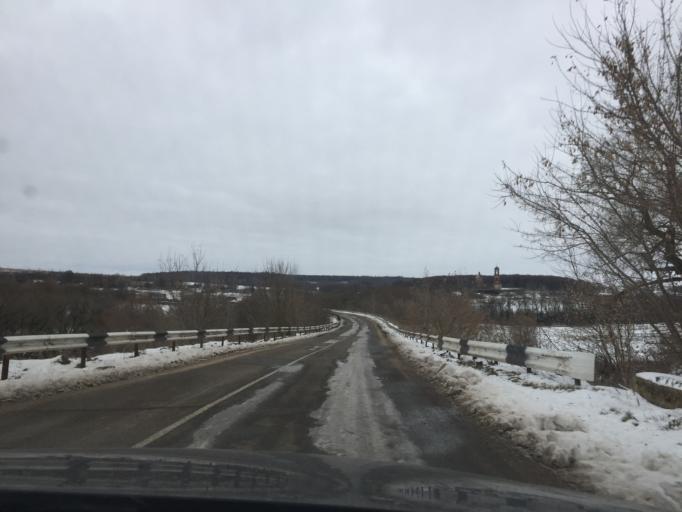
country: RU
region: Tula
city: Teploye
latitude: 53.7758
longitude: 37.6387
